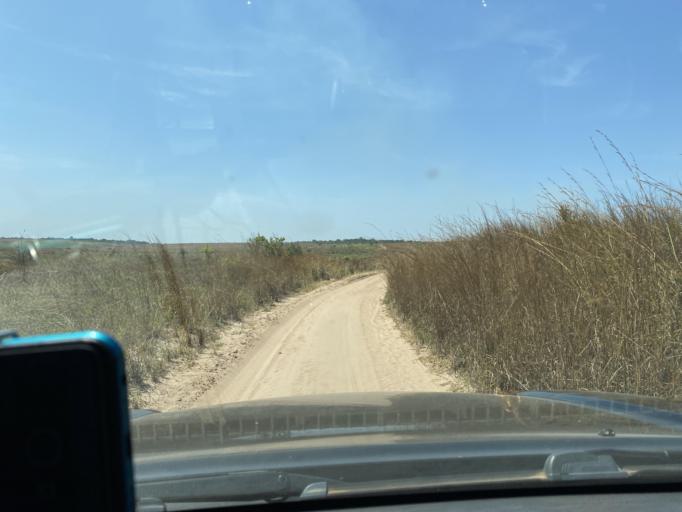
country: CD
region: Kasai-Oriental
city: Kabinda
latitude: -5.9228
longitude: 24.8371
